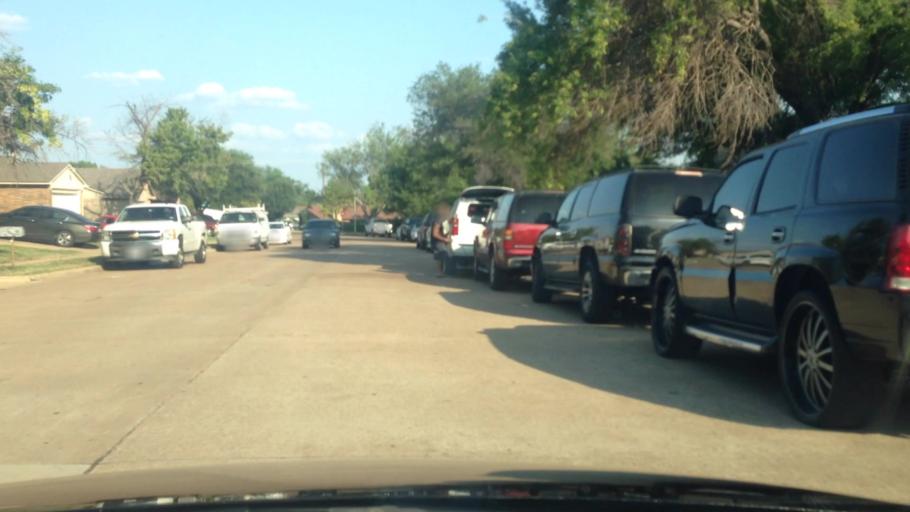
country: US
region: Texas
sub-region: Tarrant County
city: Edgecliff Village
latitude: 32.6447
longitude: -97.3418
